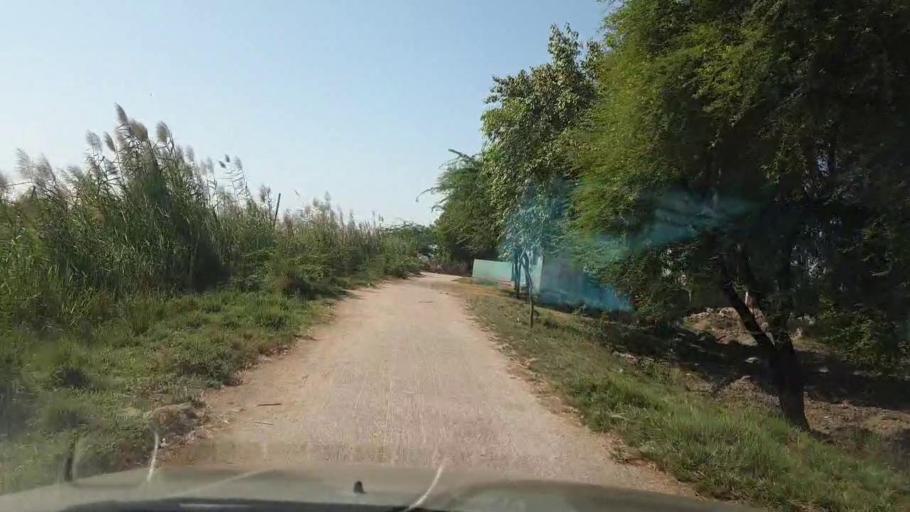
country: PK
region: Sindh
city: Thatta
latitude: 24.7206
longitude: 67.9207
